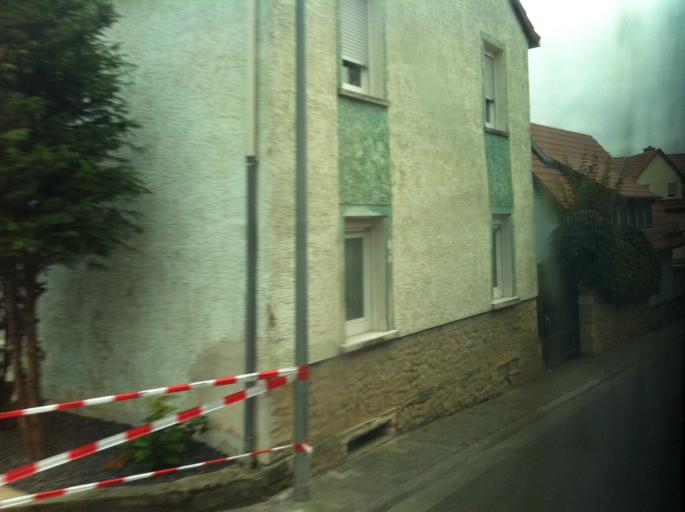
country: DE
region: Rheinland-Pfalz
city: Essenheim
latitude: 49.9333
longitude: 8.1617
